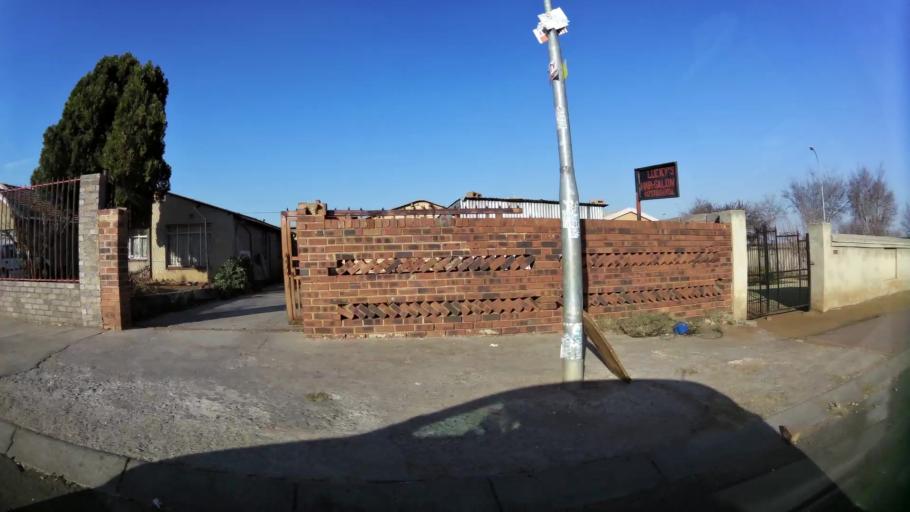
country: ZA
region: Gauteng
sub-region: City of Johannesburg Metropolitan Municipality
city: Soweto
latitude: -26.2619
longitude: 27.8841
